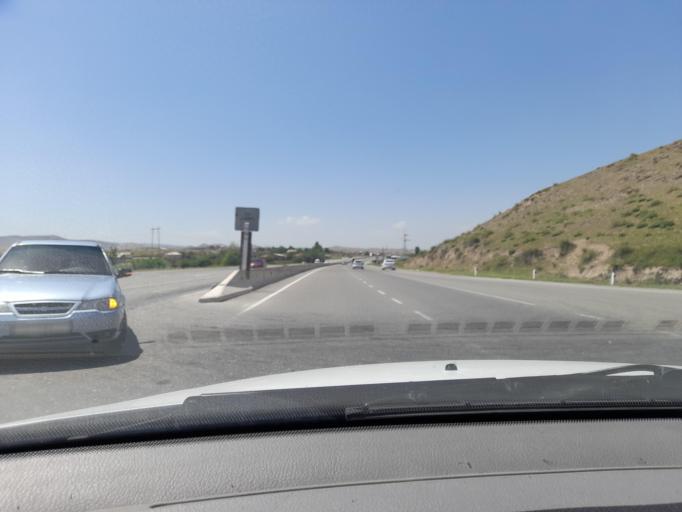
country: UZ
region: Jizzax
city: Jizzax
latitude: 40.0653
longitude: 67.8582
